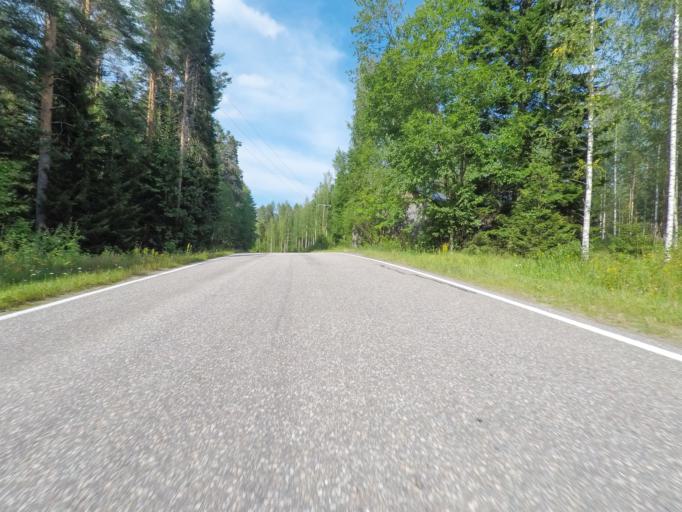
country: FI
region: Southern Savonia
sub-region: Savonlinna
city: Sulkava
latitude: 61.7624
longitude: 28.2365
